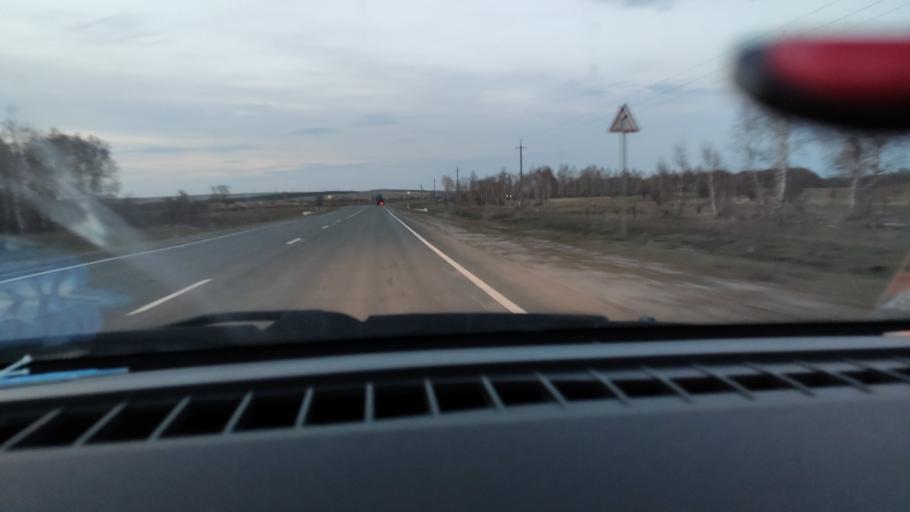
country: RU
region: Saratov
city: Sinodskoye
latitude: 52.0403
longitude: 46.7331
